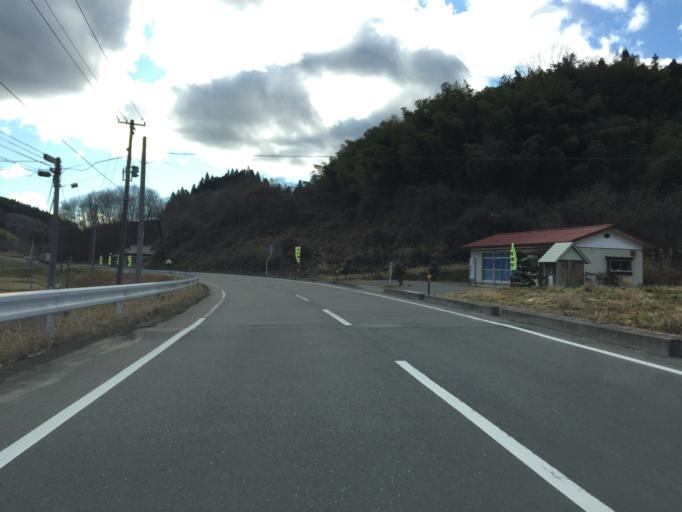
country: JP
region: Fukushima
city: Funehikimachi-funehiki
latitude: 37.5436
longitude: 140.5879
